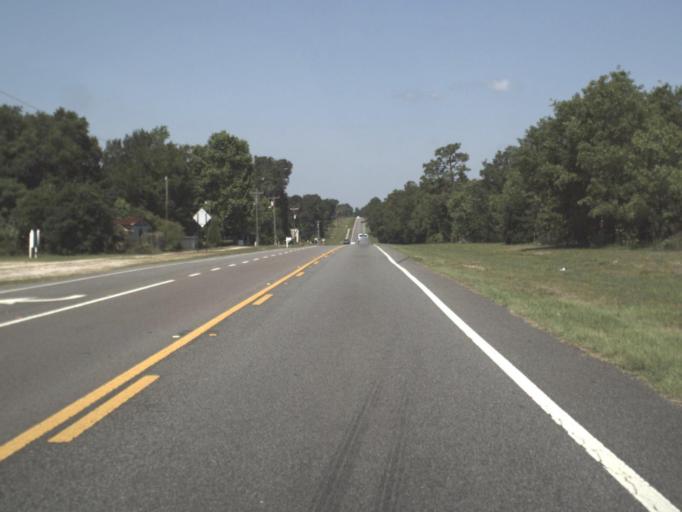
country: US
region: Florida
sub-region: Clay County
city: Asbury Lake
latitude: 29.9830
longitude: -81.7689
